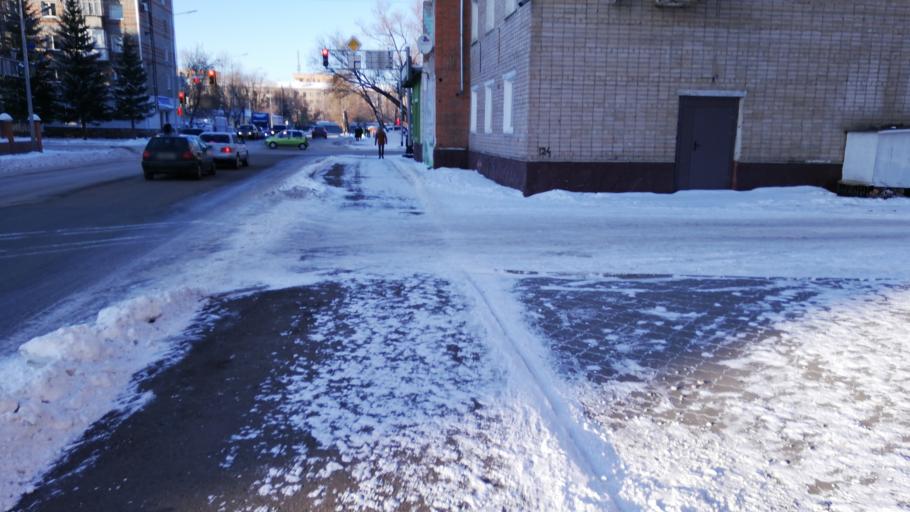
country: KZ
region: Soltustik Qazaqstan
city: Petropavlovsk
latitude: 54.8644
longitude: 69.1411
